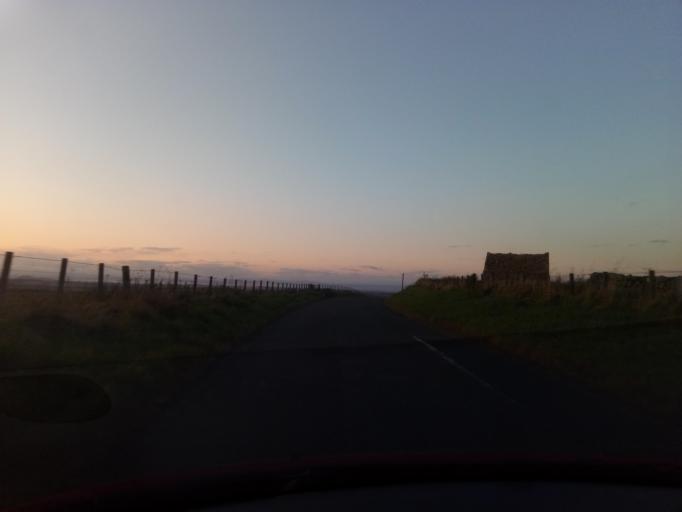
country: GB
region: Scotland
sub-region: East Lothian
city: Pencaitland
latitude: 55.8152
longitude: -2.8751
